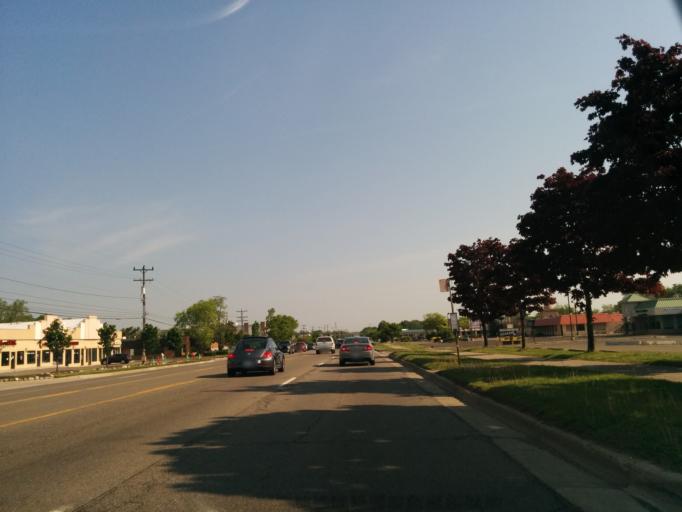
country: US
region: Michigan
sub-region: Oakland County
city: Farmington Hills
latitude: 42.5089
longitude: -83.3591
